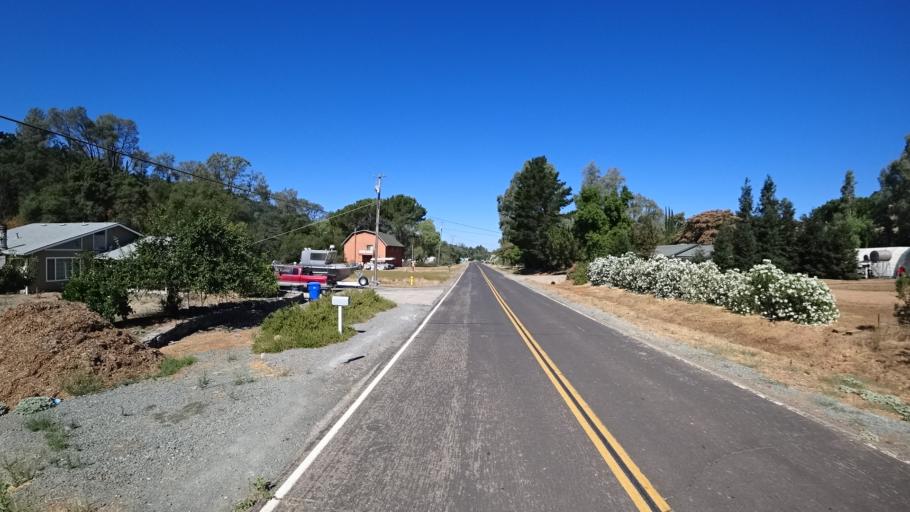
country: US
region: California
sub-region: Calaveras County
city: Rancho Calaveras
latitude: 38.1102
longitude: -120.8688
